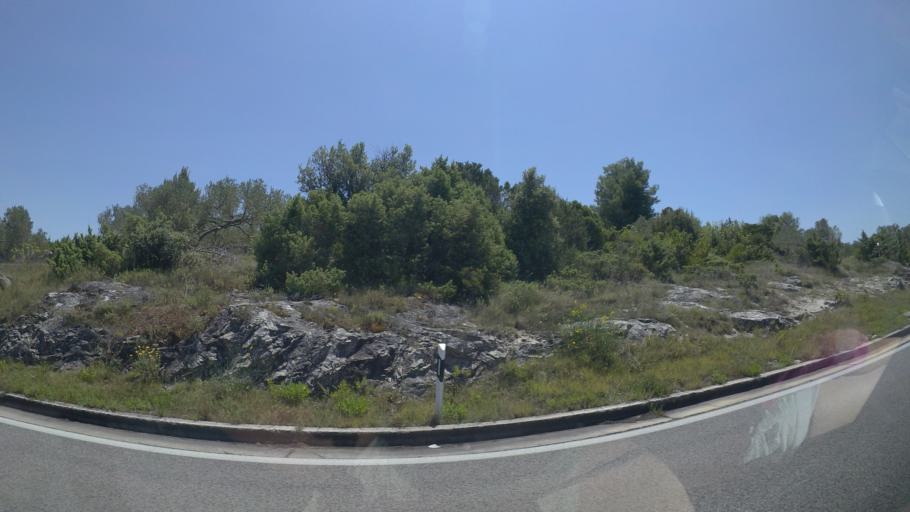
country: HR
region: Sibensko-Kniniska
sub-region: Grad Sibenik
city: Pirovac
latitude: 43.8047
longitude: 15.6658
